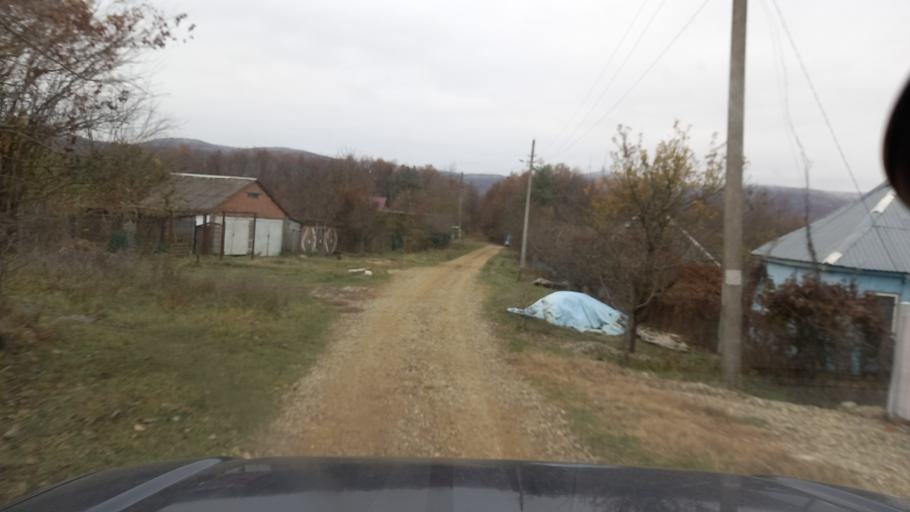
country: RU
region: Krasnodarskiy
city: Goryachiy Klyuch
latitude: 44.5127
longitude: 39.2948
